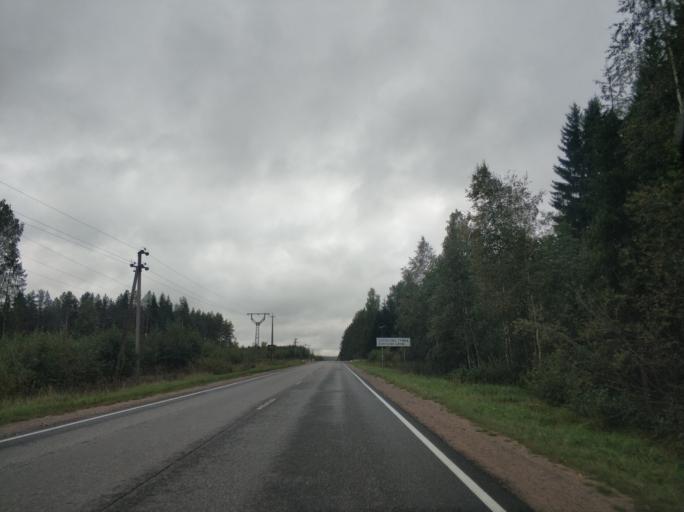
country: RU
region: Leningrad
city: Borisova Griva
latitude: 60.1002
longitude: 30.9554
